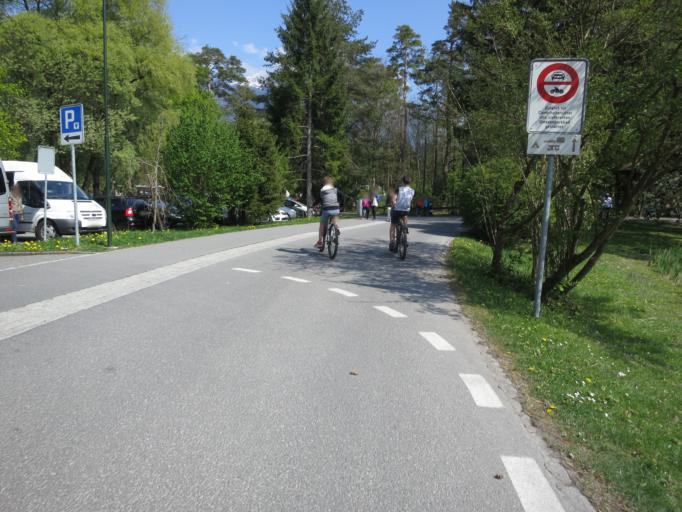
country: CH
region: Saint Gallen
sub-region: Wahlkreis Sarganserland
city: Bad Ragaz
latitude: 47.0052
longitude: 9.5098
